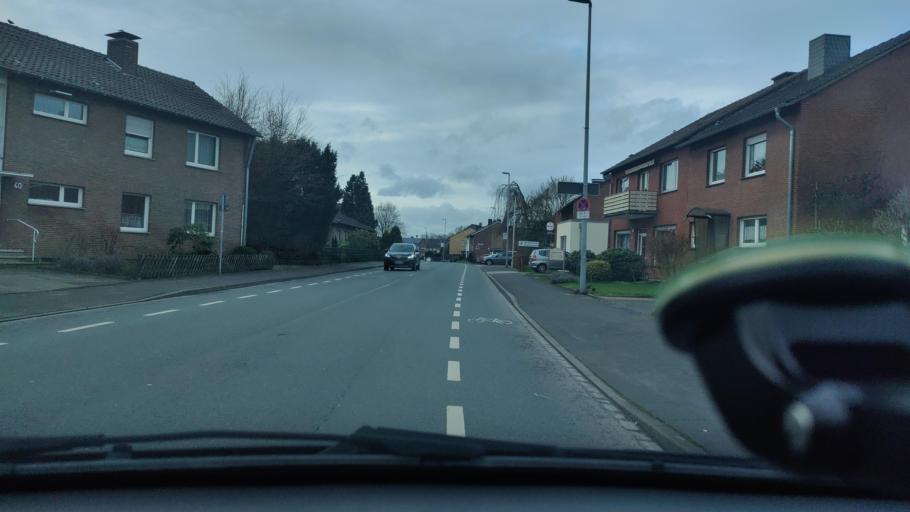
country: DE
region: North Rhine-Westphalia
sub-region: Regierungsbezirk Dusseldorf
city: Wesel
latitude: 51.6718
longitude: 6.6499
